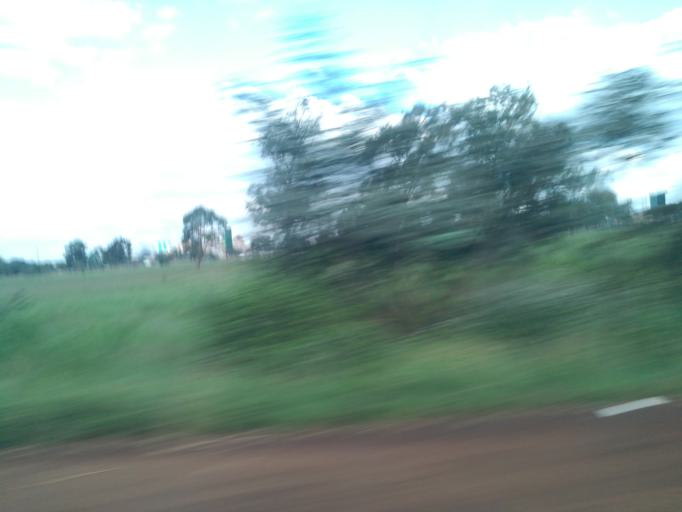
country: KE
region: Nairobi Area
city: Thika
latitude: -1.0409
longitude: 37.0590
